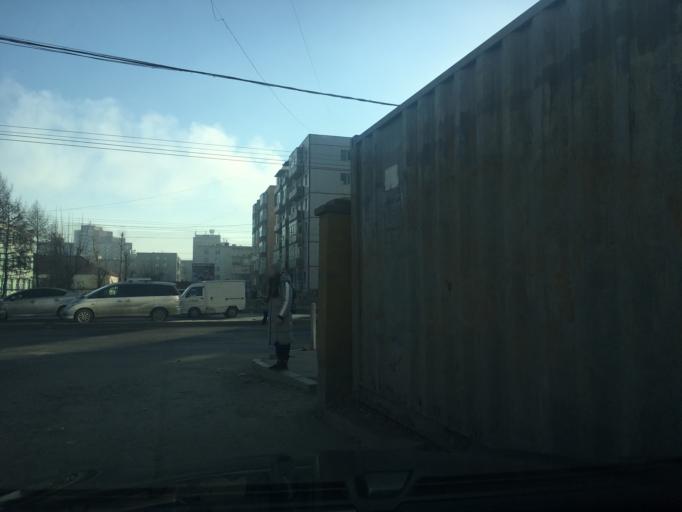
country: MN
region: Ulaanbaatar
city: Ulaanbaatar
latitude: 47.9145
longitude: 106.8752
